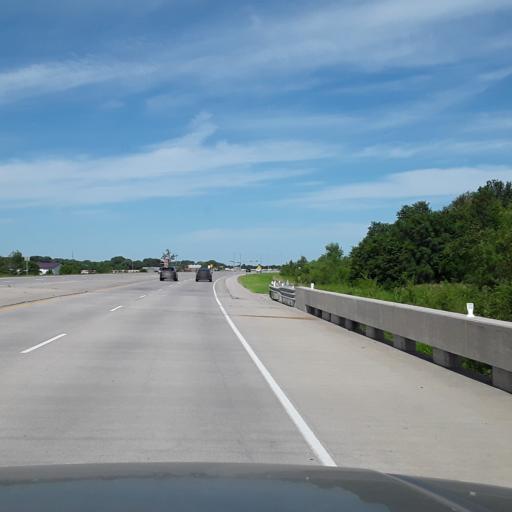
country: US
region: Nebraska
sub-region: Lancaster County
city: Lincoln
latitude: 40.8800
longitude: -96.7758
